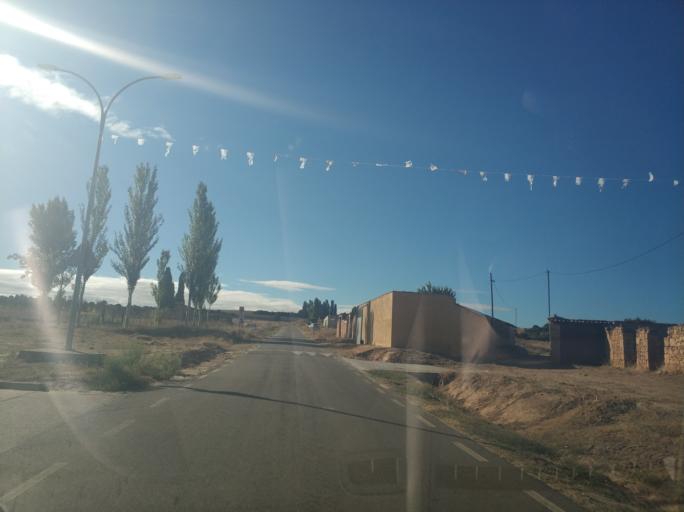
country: ES
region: Castille and Leon
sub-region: Provincia de Burgos
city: San Juan del Monte
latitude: 41.6810
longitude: -3.5242
